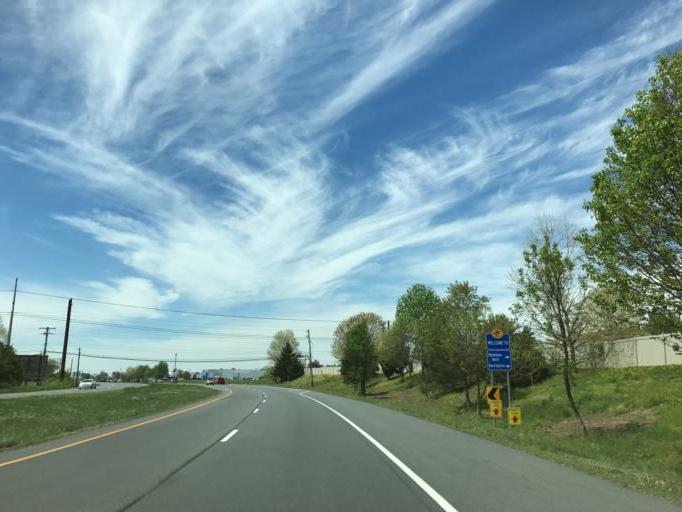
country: US
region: Delaware
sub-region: New Castle County
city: Glasgow
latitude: 39.6066
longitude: -75.7815
